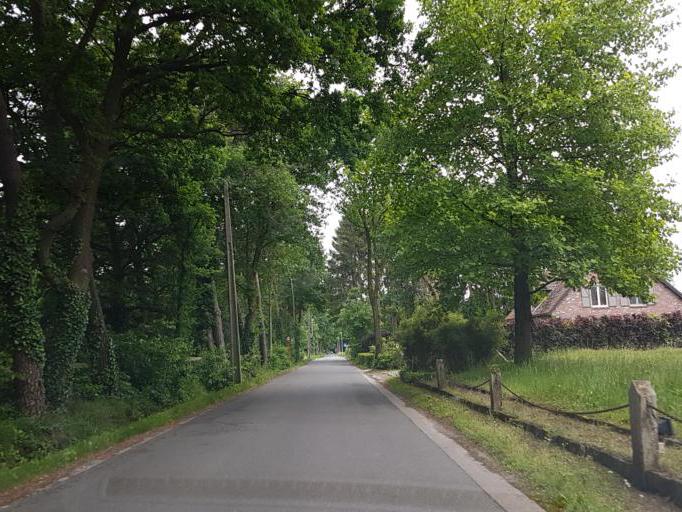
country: BE
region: Flanders
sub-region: Provincie Antwerpen
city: Zoersel
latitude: 51.2739
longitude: 4.6817
